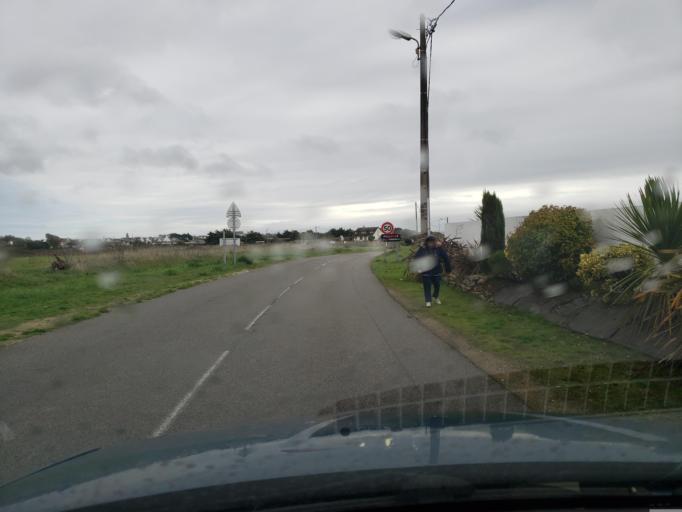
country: FR
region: Brittany
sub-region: Departement du Finistere
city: Guilvinec
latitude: 47.8048
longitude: -4.3036
